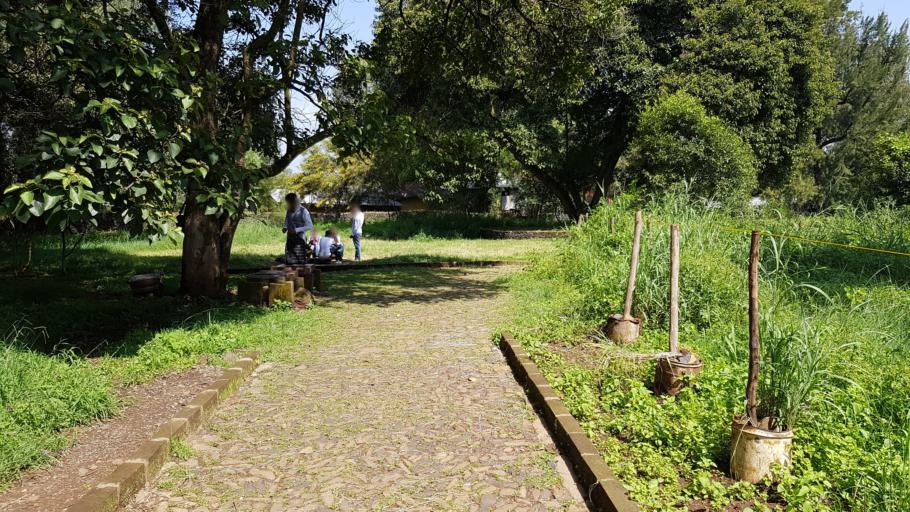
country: ET
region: Amhara
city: Gondar
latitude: 12.6071
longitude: 37.4695
